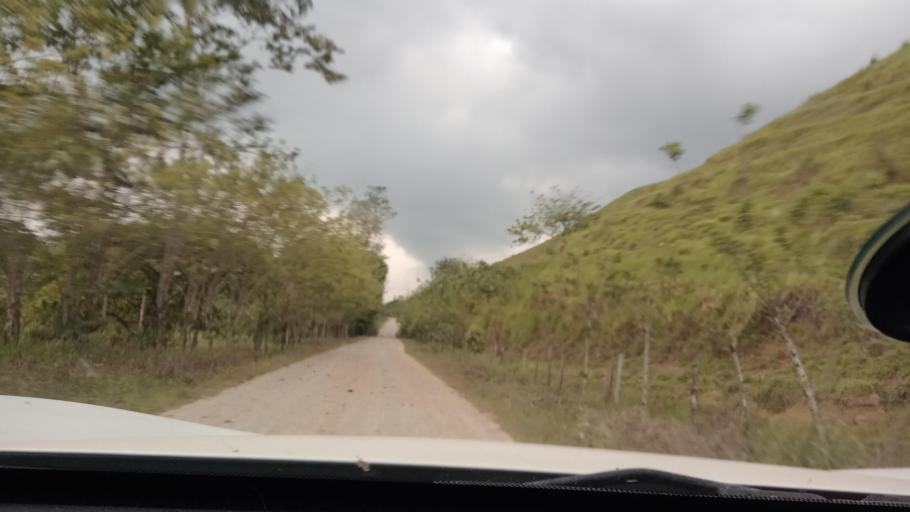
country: MX
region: Tabasco
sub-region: Huimanguillo
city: Francisco Rueda
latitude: 17.4393
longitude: -94.0623
